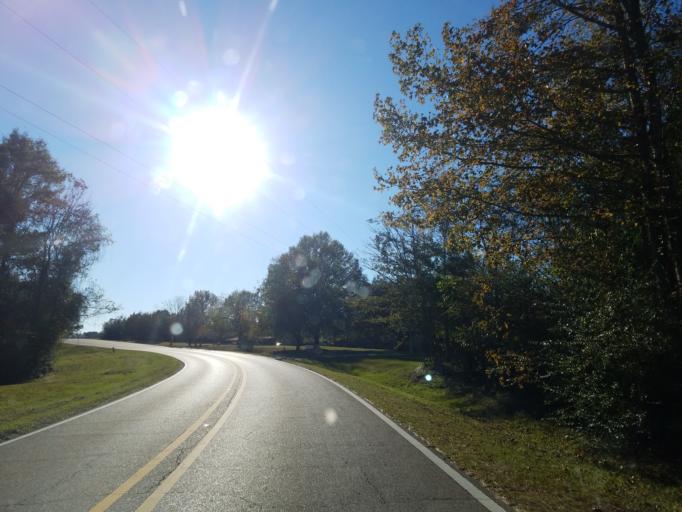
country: US
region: Mississippi
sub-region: Forrest County
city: Hattiesburg
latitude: 31.2456
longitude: -89.3003
